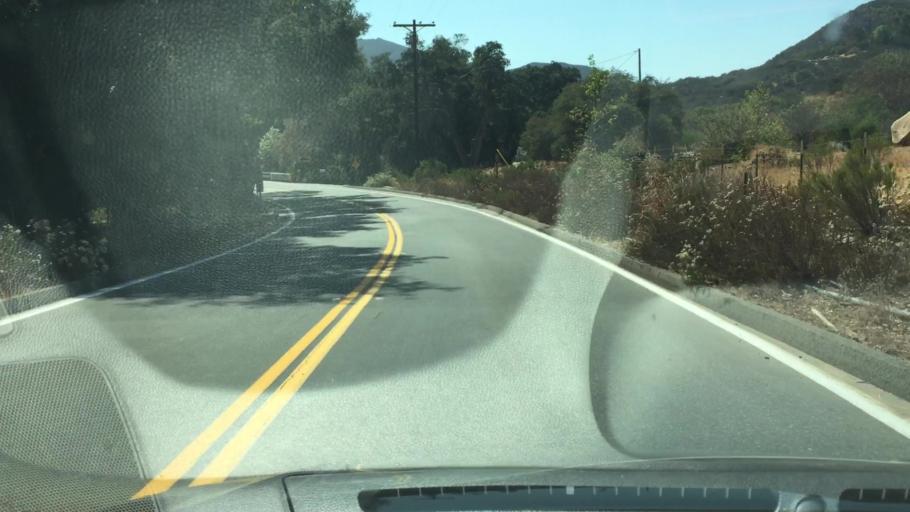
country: US
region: California
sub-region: San Diego County
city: Alpine
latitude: 32.7549
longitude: -116.7721
